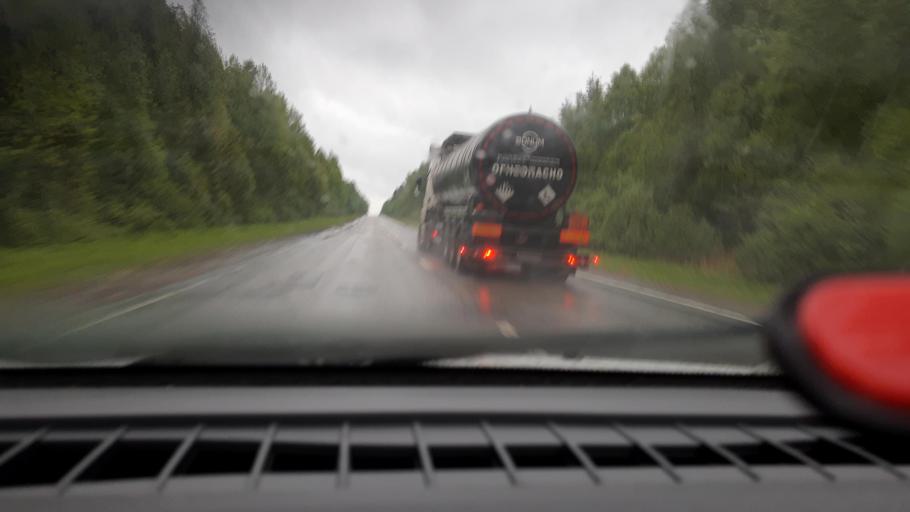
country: RU
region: Nizjnij Novgorod
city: Vladimirskoye
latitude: 56.9362
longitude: 45.0741
